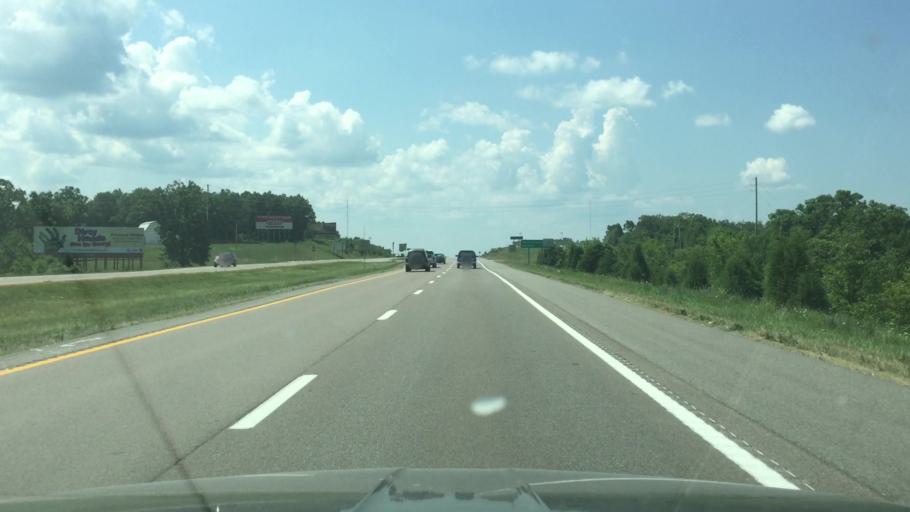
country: US
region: Missouri
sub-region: Miller County
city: Eldon
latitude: 38.2977
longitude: -92.5802
